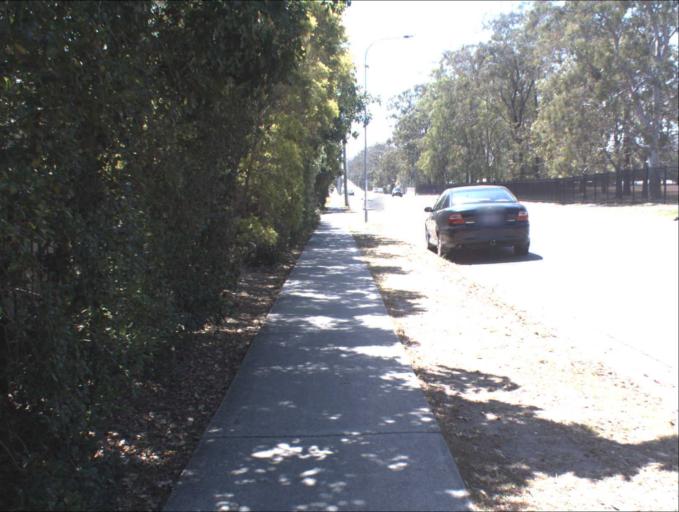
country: AU
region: Queensland
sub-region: Gold Coast
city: Yatala
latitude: -27.7027
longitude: 153.2144
